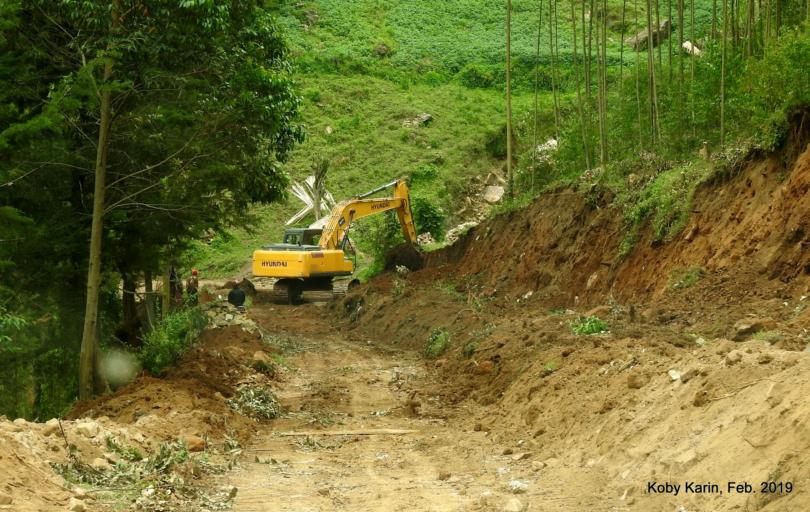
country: UG
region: Western Region
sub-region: Kisoro District
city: Kisoro
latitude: -1.1348
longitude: 29.7357
